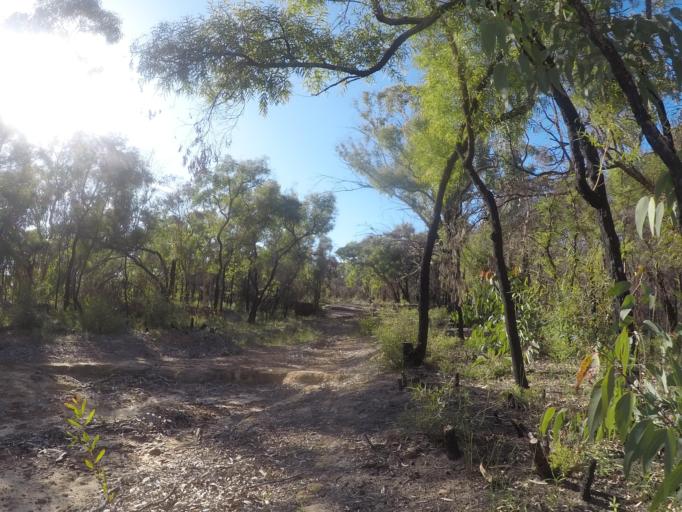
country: AU
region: New South Wales
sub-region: Hornsby Shire
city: Glenorie
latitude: -33.3420
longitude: 151.0603
